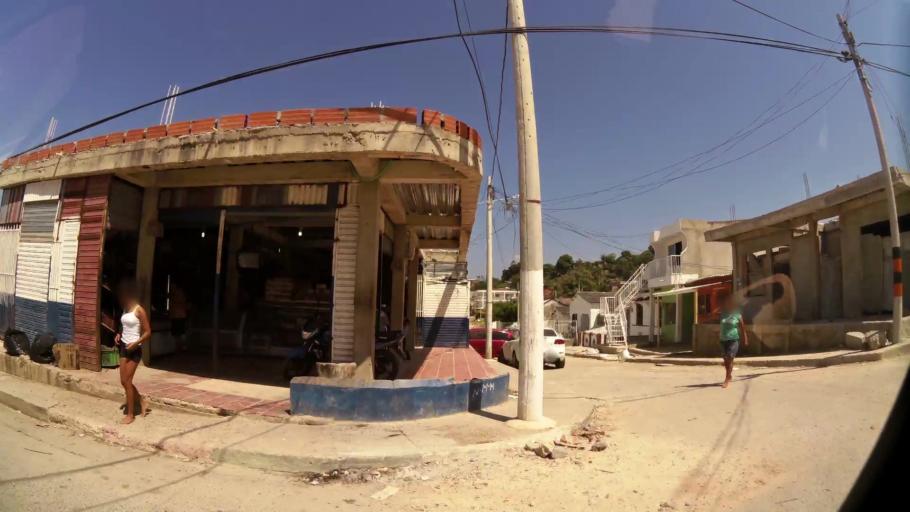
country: CO
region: Bolivar
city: Cartagena
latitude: 10.4313
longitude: -75.5291
